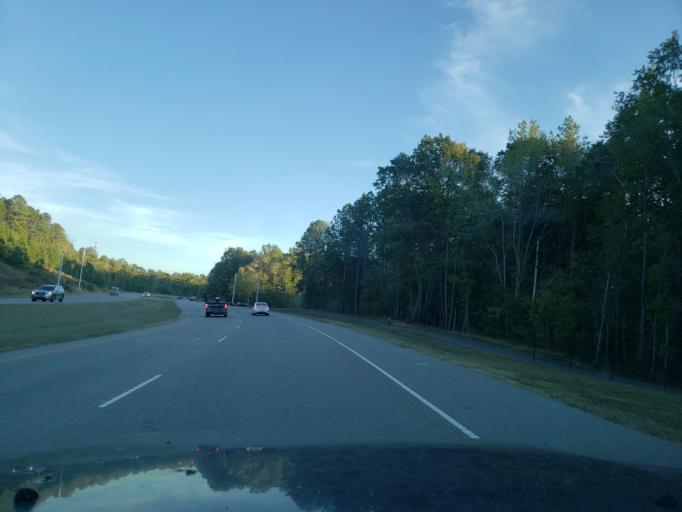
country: US
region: North Carolina
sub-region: Wake County
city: Morrisville
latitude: 35.8474
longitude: -78.8579
